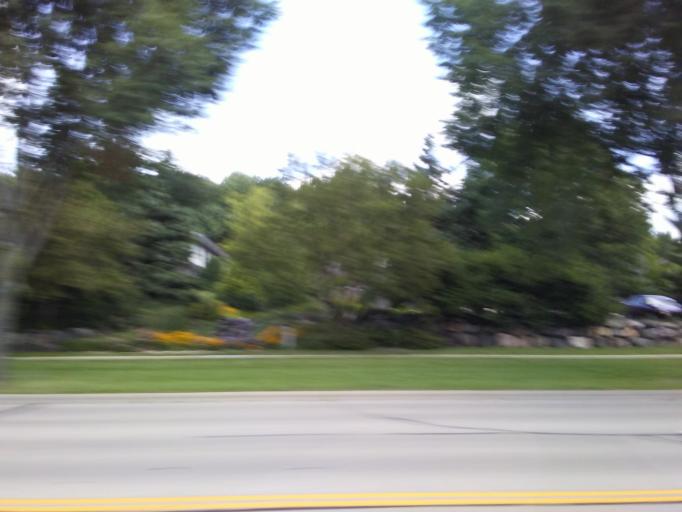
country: US
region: Wisconsin
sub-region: Dane County
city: Verona
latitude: 43.0316
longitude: -89.5000
